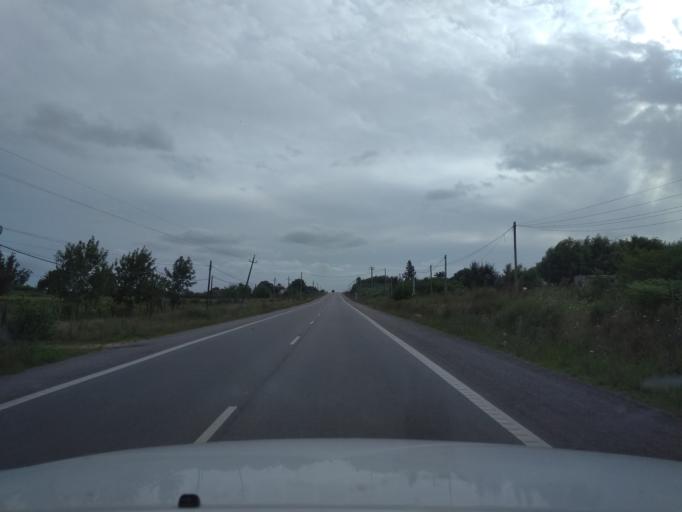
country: UY
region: Canelones
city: Joaquin Suarez
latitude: -34.6971
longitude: -56.0358
